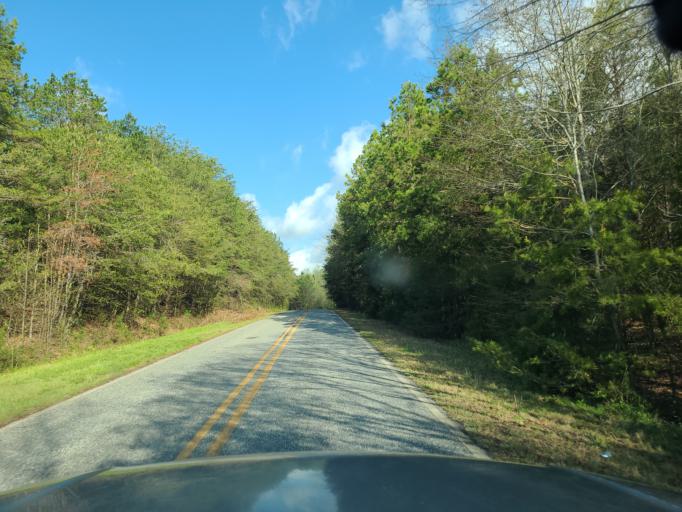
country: US
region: North Carolina
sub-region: Rutherford County
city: Forest City
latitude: 35.4217
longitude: -81.8232
